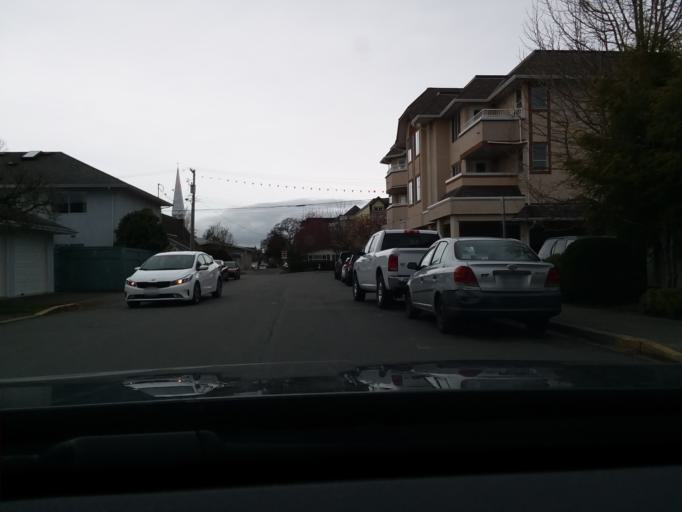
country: CA
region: British Columbia
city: North Saanich
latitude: 48.6468
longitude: -123.3970
